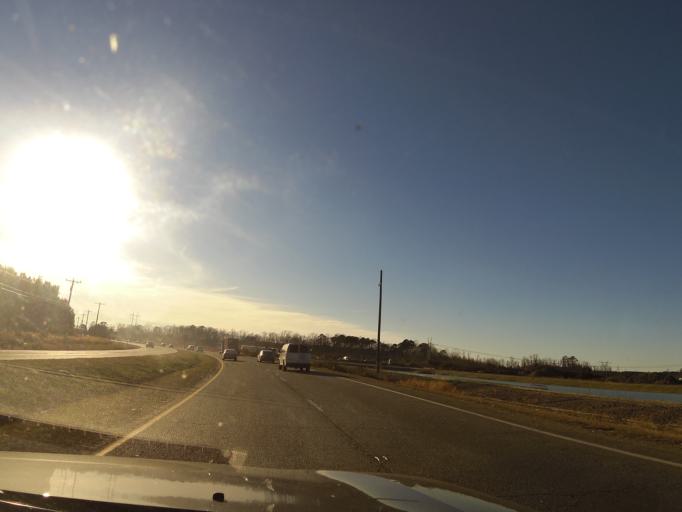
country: US
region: Virginia
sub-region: City of Suffolk
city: South Suffolk
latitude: 36.7129
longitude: -76.6733
